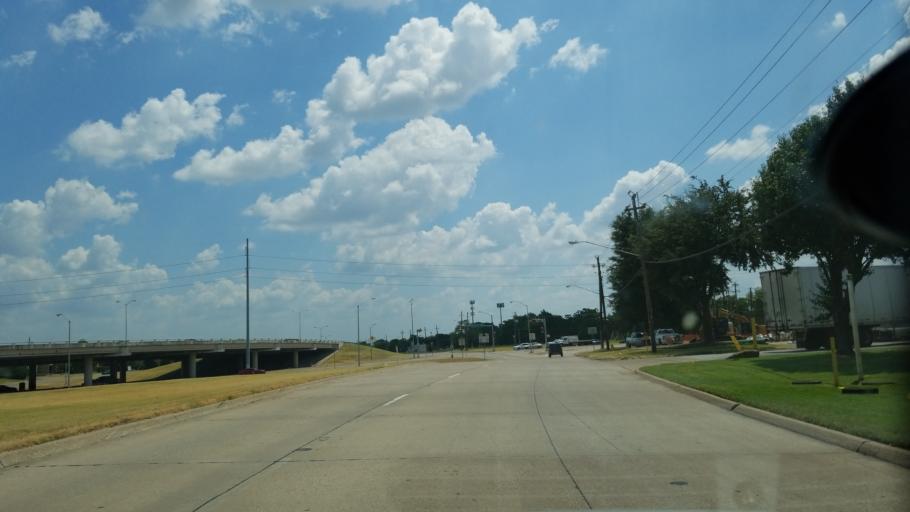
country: US
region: Texas
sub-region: Dallas County
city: Duncanville
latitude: 32.6911
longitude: -96.8931
